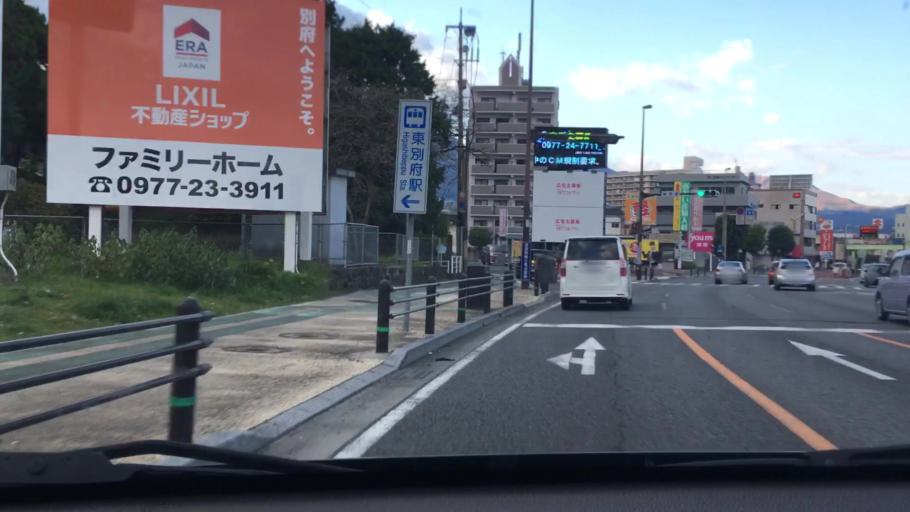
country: JP
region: Oita
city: Beppu
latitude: 33.2677
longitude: 131.5115
